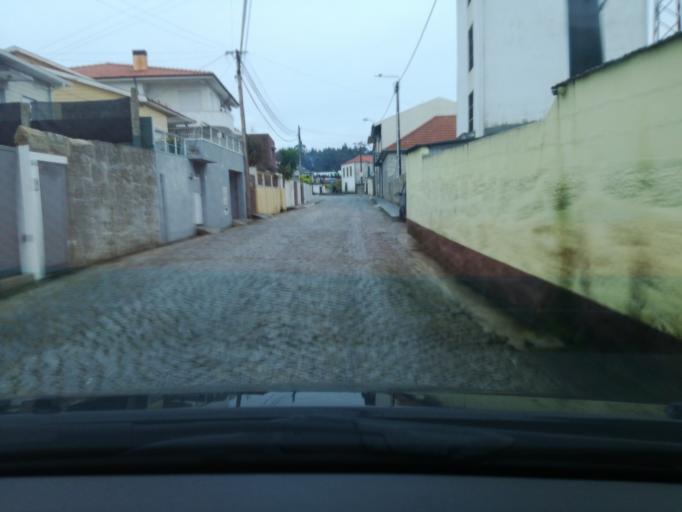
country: PT
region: Porto
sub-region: Maia
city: Gemunde
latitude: 41.2666
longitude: -8.6427
